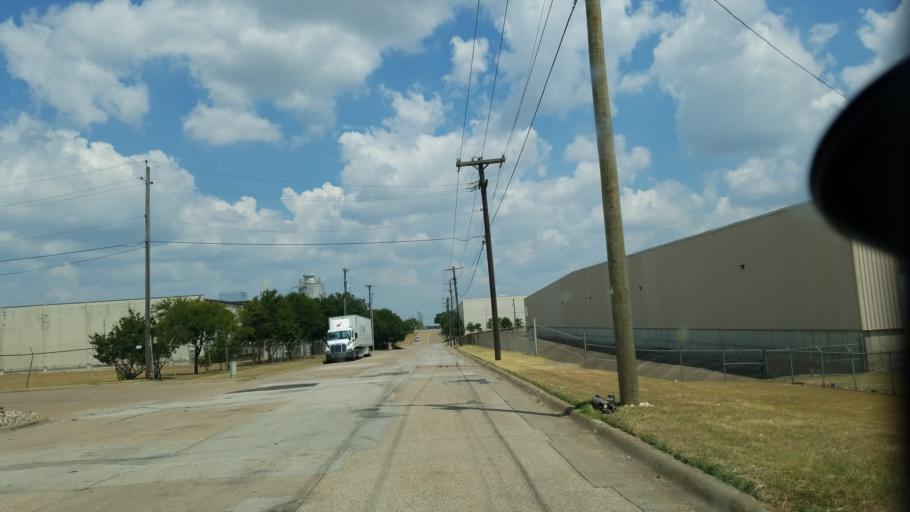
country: US
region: Texas
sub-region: Dallas County
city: Duncanville
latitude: 32.6891
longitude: -96.8986
